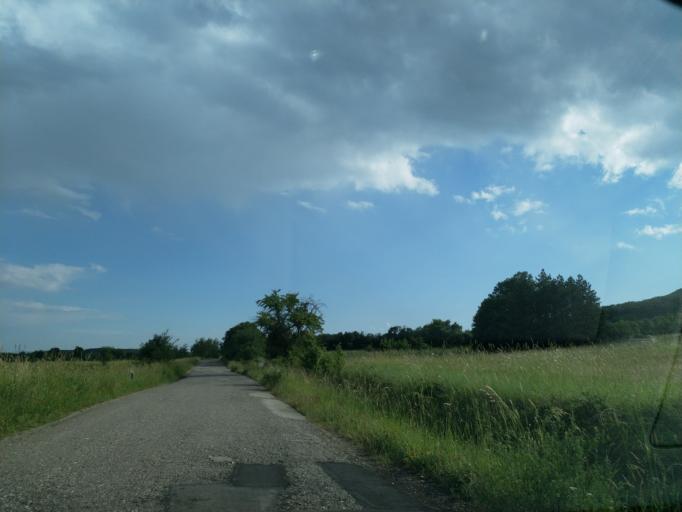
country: RS
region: Central Serbia
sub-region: Borski Okrug
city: Bor
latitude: 43.9842
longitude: 21.9736
